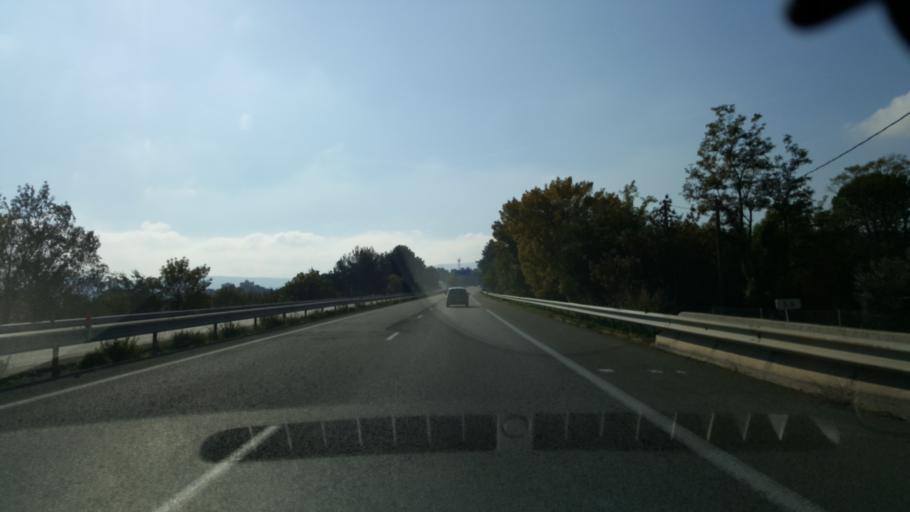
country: FR
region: Provence-Alpes-Cote d'Azur
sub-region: Departement des Bouches-du-Rhone
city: Aubagne
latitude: 43.3087
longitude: 5.5788
